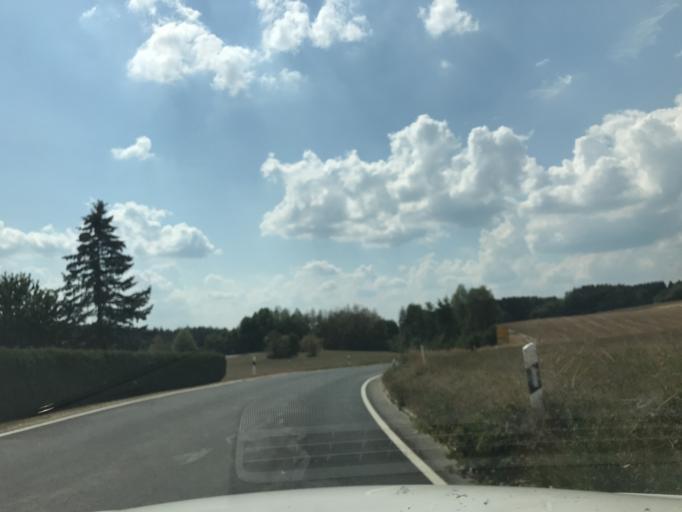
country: DE
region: Bavaria
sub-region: Upper Palatinate
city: Auerbach
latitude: 49.7353
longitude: 11.6661
